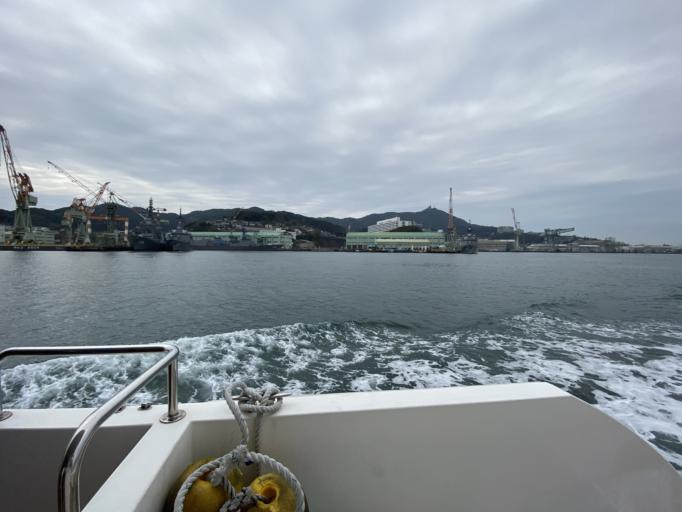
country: JP
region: Nagasaki
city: Nagasaki-shi
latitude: 32.7342
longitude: 129.8603
